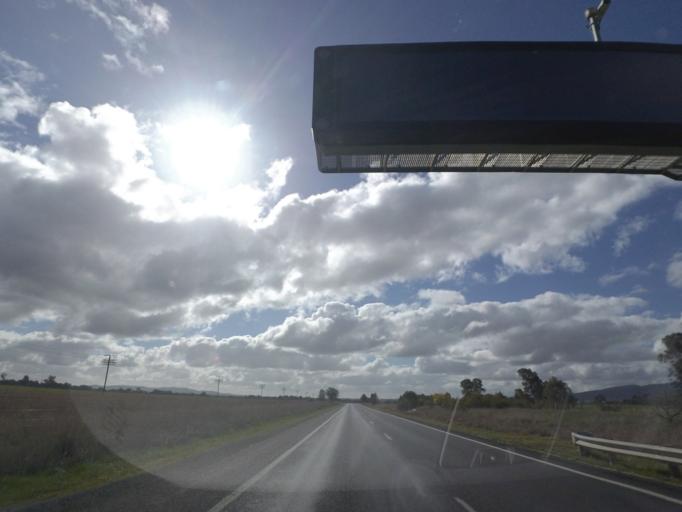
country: AU
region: New South Wales
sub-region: Greater Hume Shire
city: Jindera
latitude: -35.9453
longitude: 147.0033
